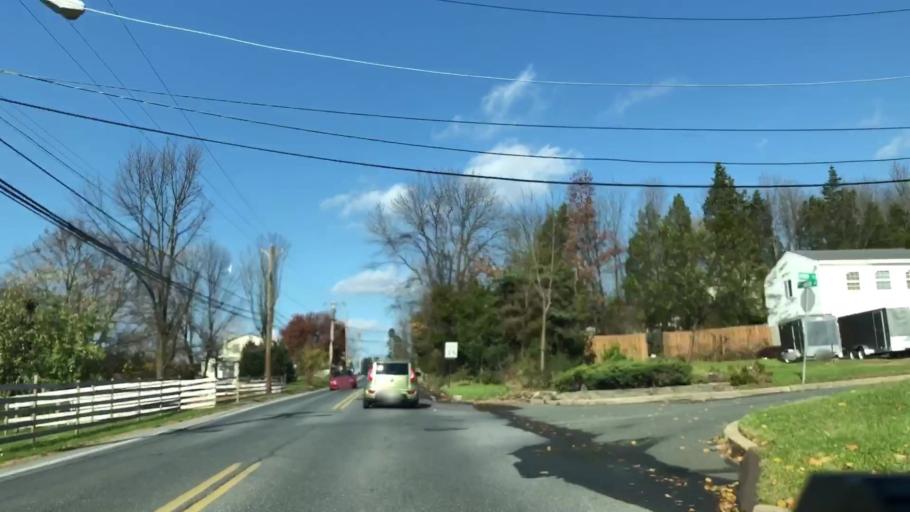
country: US
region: Pennsylvania
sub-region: Montgomery County
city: Halfway House
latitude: 40.2746
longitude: -75.6416
